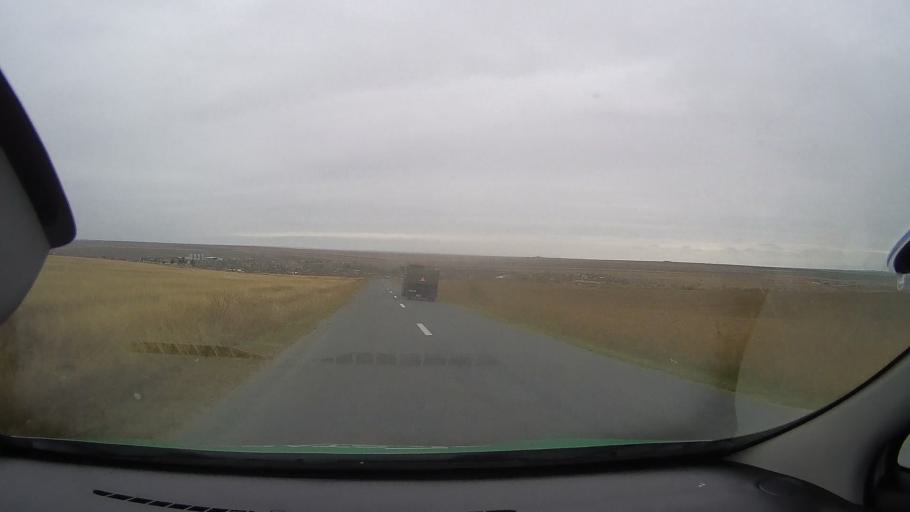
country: RO
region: Constanta
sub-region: Comuna Pantelimon
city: Pantelimon
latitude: 44.5931
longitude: 28.3225
